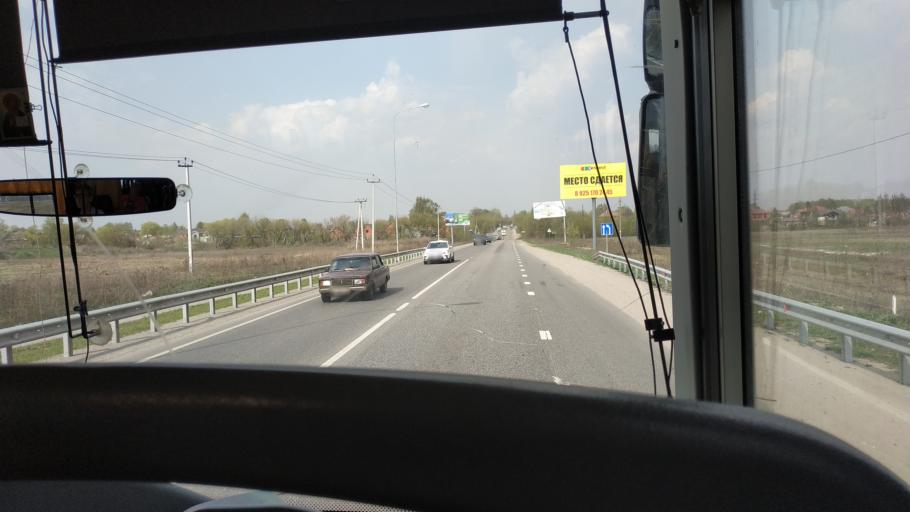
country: RU
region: Moskovskaya
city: Tomilino
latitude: 55.6234
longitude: 37.9247
